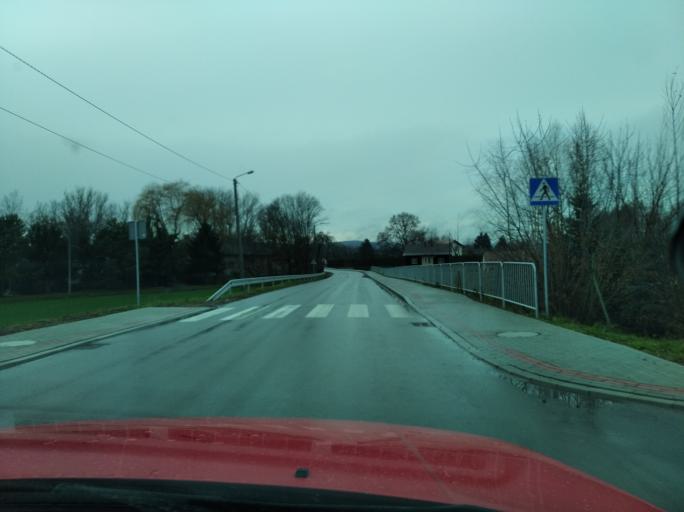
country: PL
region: Subcarpathian Voivodeship
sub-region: Powiat rzeszowski
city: Siedliska
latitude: 49.9508
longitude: 21.9315
